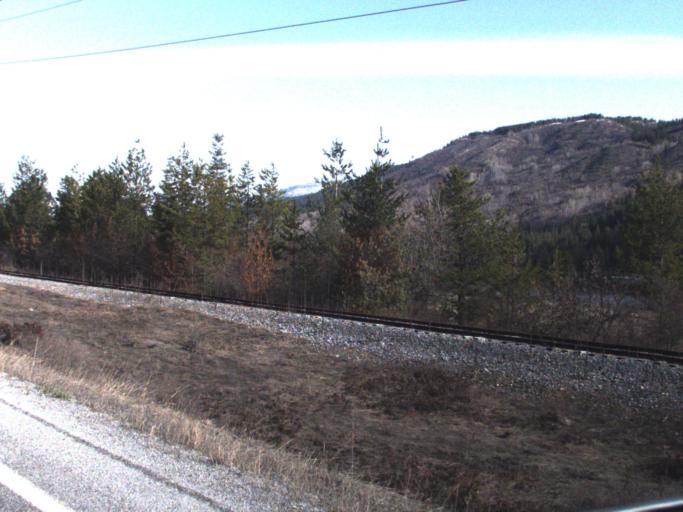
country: US
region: Washington
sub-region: Stevens County
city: Chewelah
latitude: 48.6399
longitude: -117.3721
